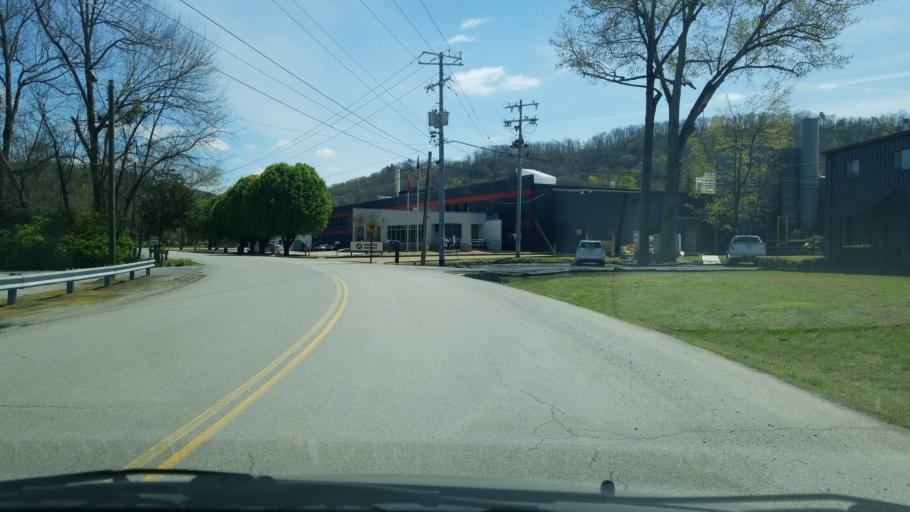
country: US
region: Tennessee
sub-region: Hamilton County
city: Collegedale
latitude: 35.0776
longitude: -85.0589
